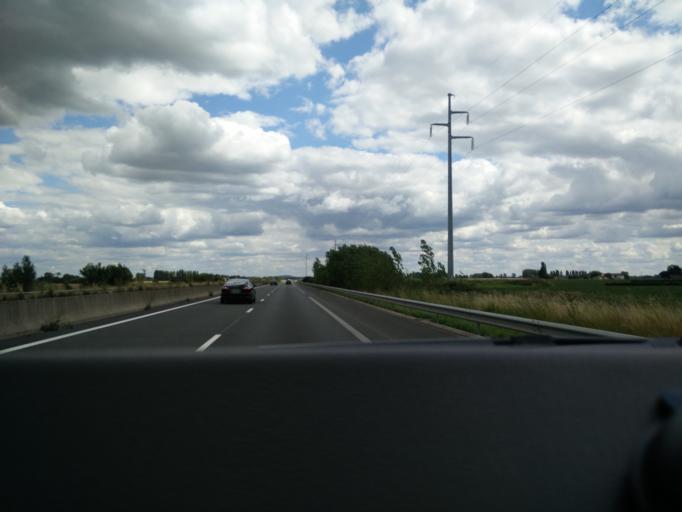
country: FR
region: Nord-Pas-de-Calais
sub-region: Departement du Nord
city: Wormhout
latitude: 50.9010
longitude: 2.4965
